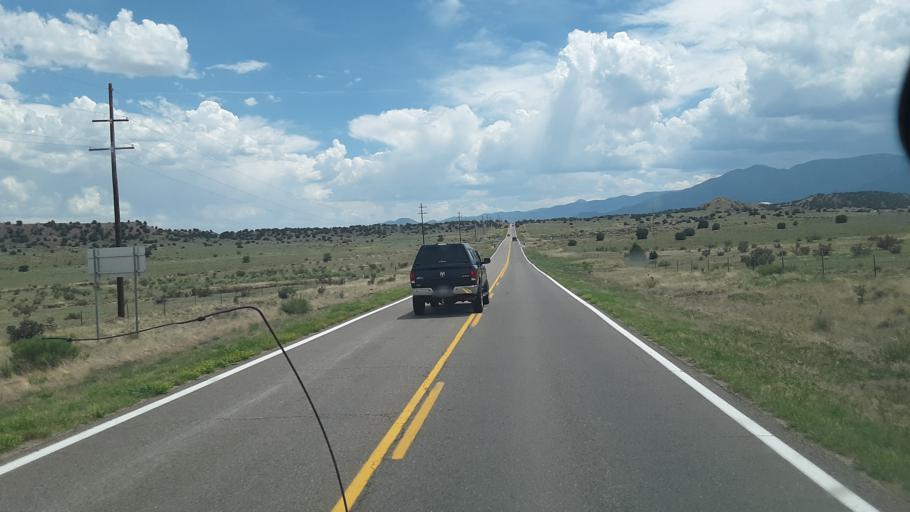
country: US
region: Colorado
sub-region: Fremont County
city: Florence
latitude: 38.3420
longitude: -105.1068
